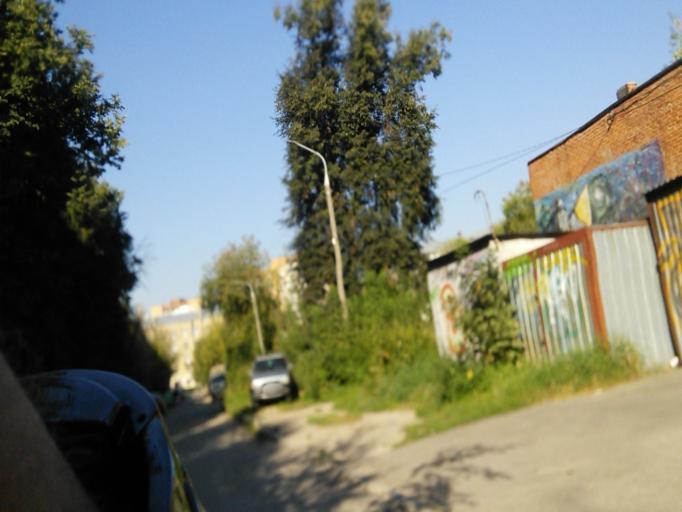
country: RU
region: Moskovskaya
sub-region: Podol'skiy Rayon
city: Podol'sk
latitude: 55.4330
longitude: 37.5605
